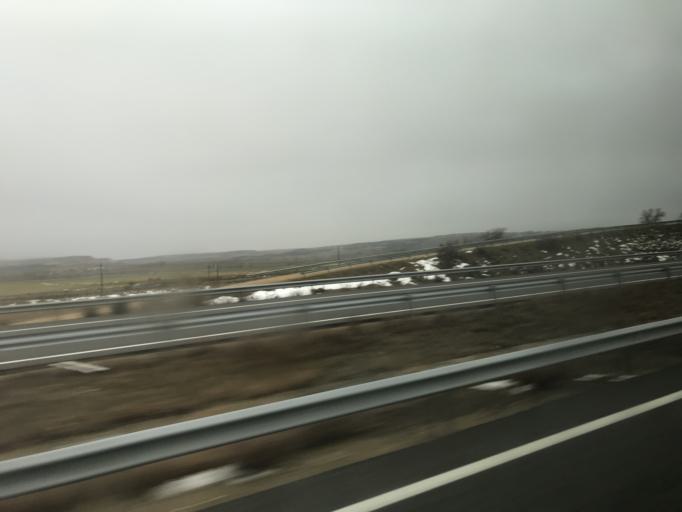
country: ES
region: Castille and Leon
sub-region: Provincia de Burgos
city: Villazopeque
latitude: 42.1893
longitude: -4.0349
